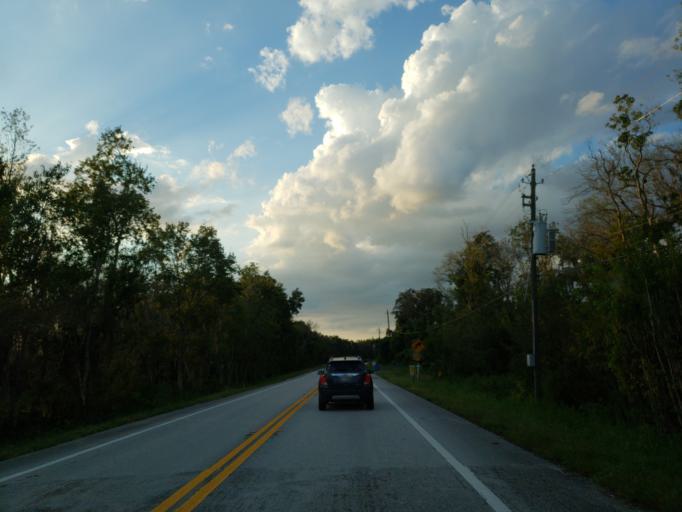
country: US
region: Florida
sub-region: Pasco County
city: Odessa
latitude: 28.1593
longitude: -82.5851
